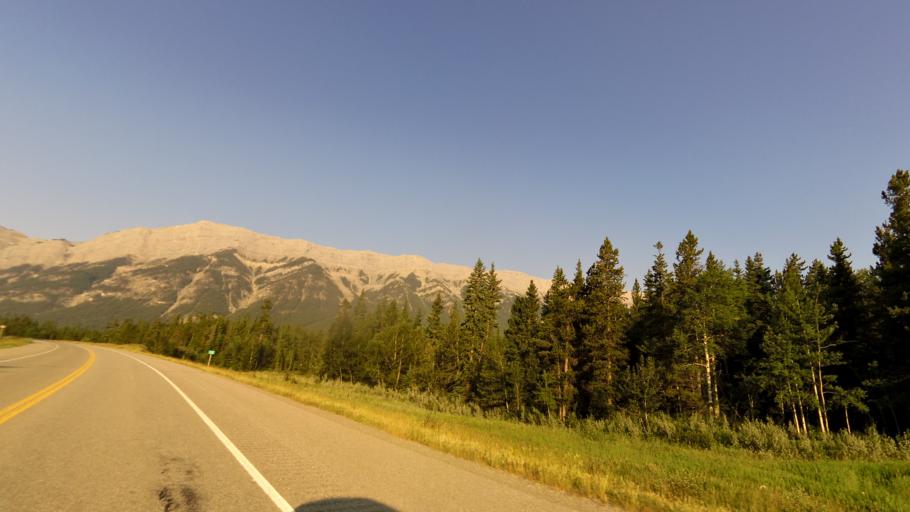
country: CA
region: Alberta
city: Lake Louise
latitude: 52.2131
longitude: -116.4762
